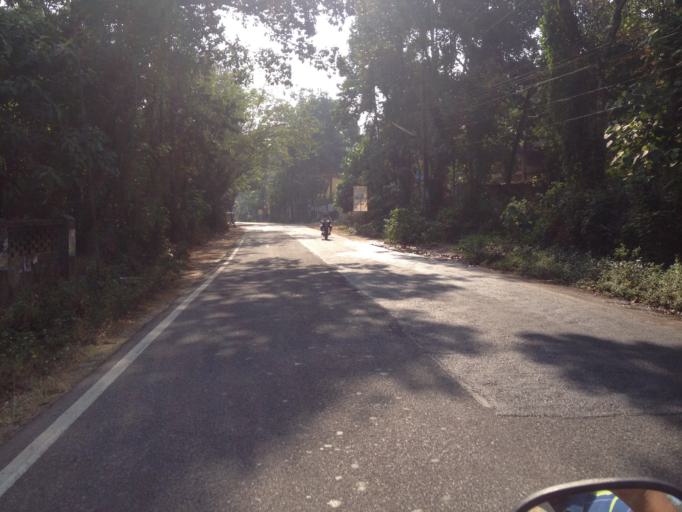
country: IN
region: Kerala
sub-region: Pattanamtitta
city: Adur
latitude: 9.1512
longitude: 76.7458
